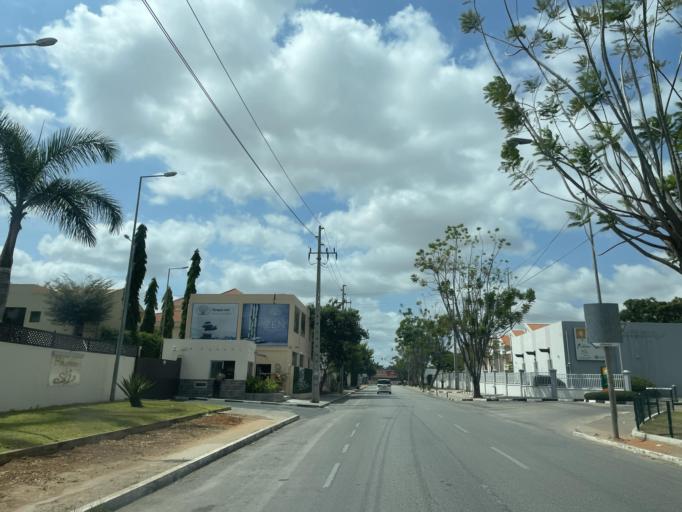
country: AO
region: Luanda
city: Luanda
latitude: -8.9218
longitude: 13.1809
